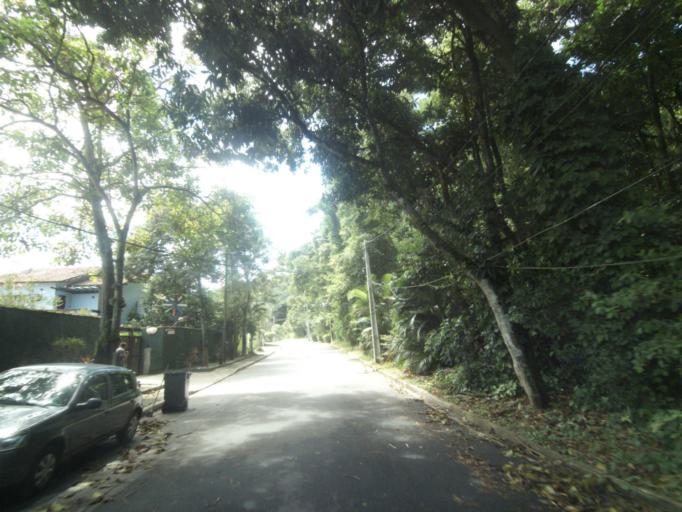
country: BR
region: Rio de Janeiro
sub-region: Niteroi
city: Niteroi
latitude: -22.9550
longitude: -43.0235
